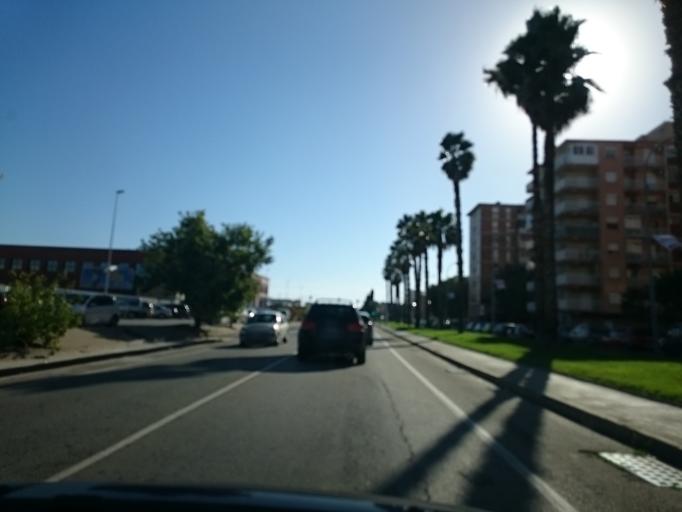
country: ES
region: Catalonia
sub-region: Provincia de Barcelona
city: Sant Boi de Llobregat
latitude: 41.3319
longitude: 2.0417
